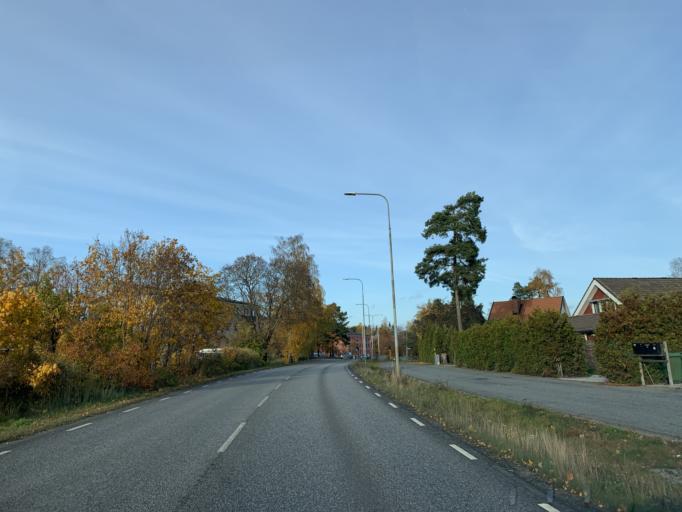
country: SE
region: Stockholm
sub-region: Haninge Kommun
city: Haninge
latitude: 59.1833
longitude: 18.1811
